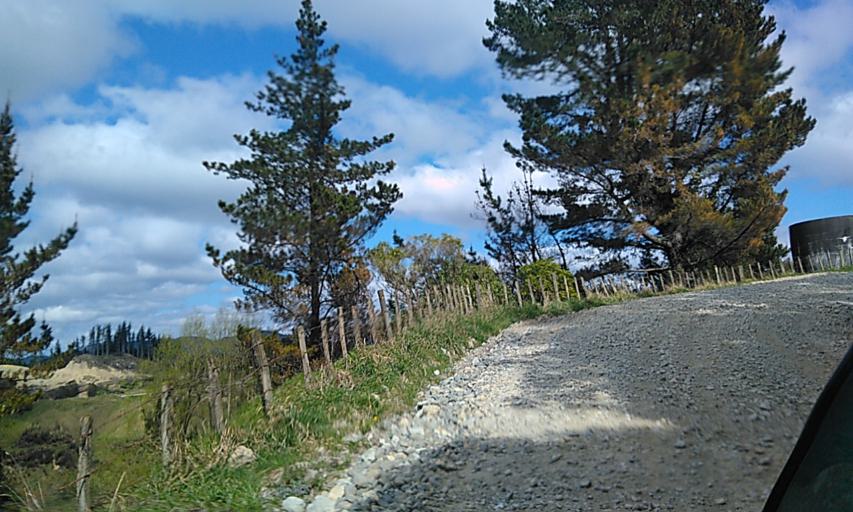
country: NZ
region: Gisborne
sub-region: Gisborne District
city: Gisborne
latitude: -38.3160
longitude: 178.0850
